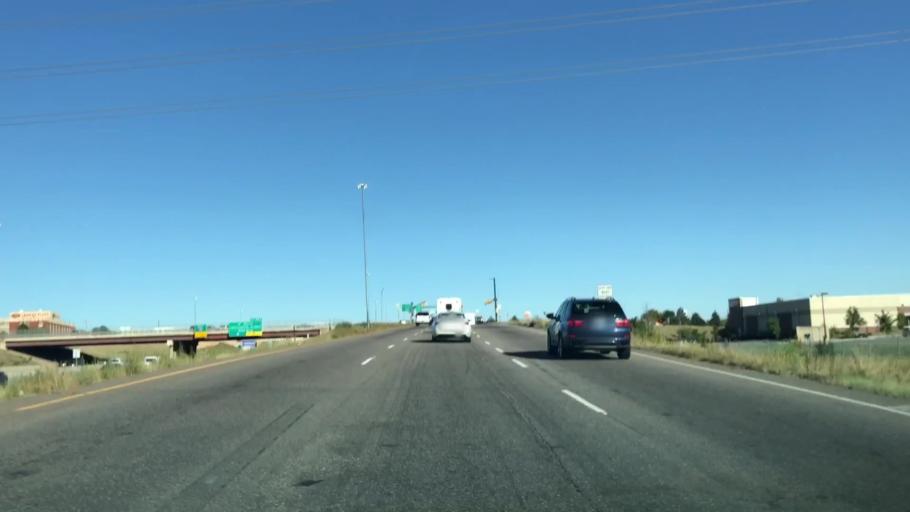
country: US
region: Colorado
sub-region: Adams County
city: Aurora
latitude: 39.7708
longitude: -104.8125
